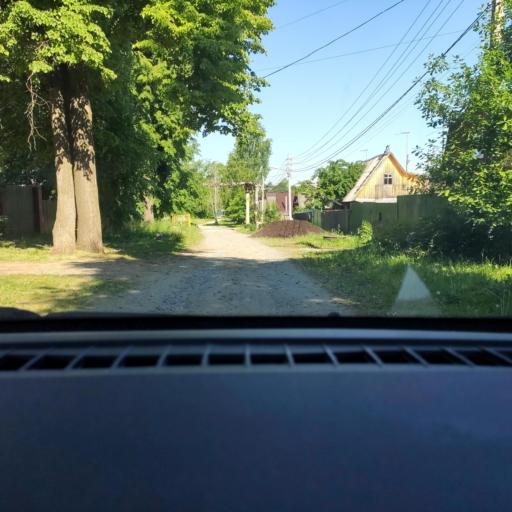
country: RU
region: Perm
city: Perm
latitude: 58.0820
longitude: 56.3919
